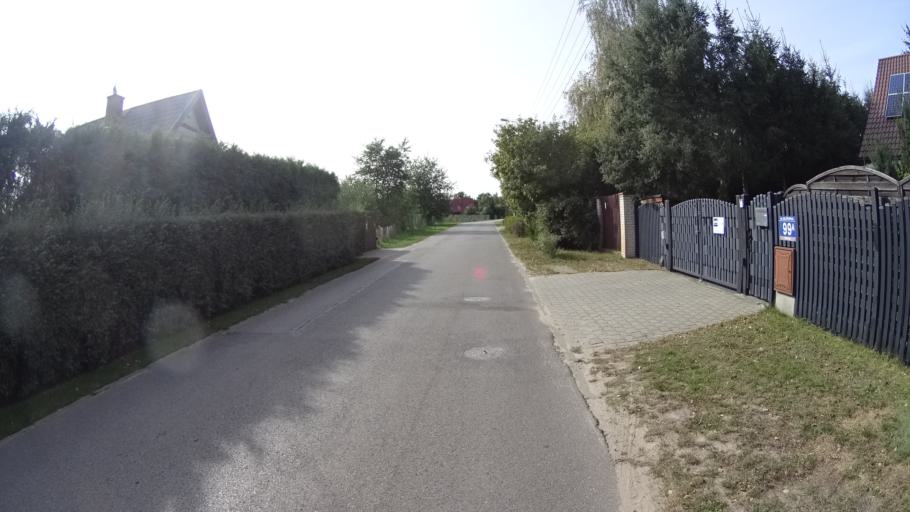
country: PL
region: Masovian Voivodeship
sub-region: Powiat legionowski
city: Serock
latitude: 52.4753
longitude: 21.0867
